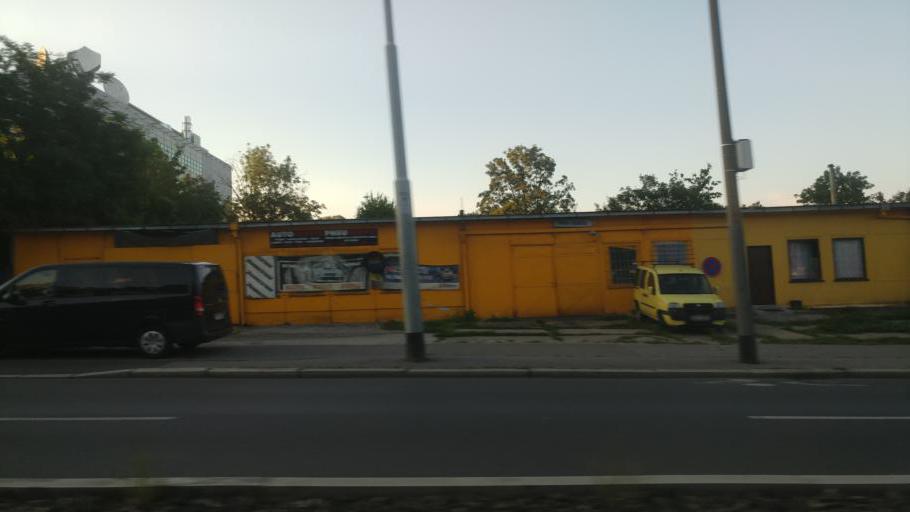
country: CZ
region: Praha
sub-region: Praha 8
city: Liben
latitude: 50.0778
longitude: 14.4793
